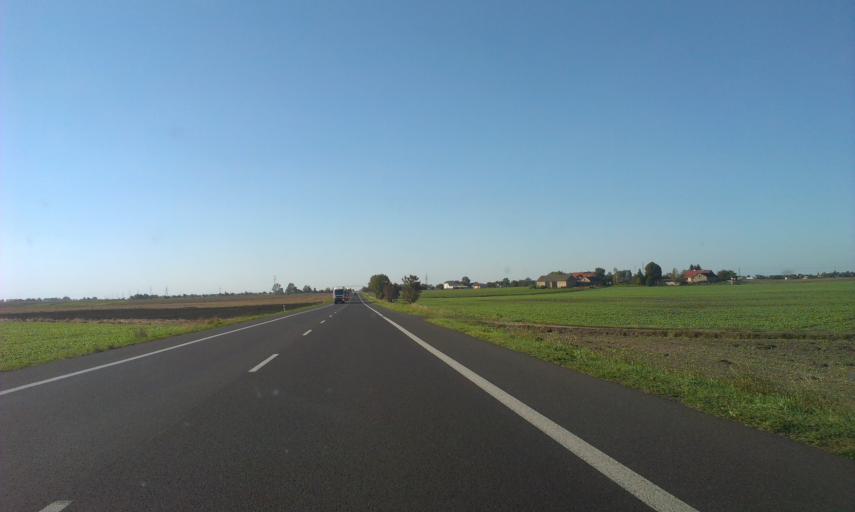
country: PL
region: Kujawsko-Pomorskie
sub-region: Powiat torunski
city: Chelmza
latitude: 53.1615
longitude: 18.5954
